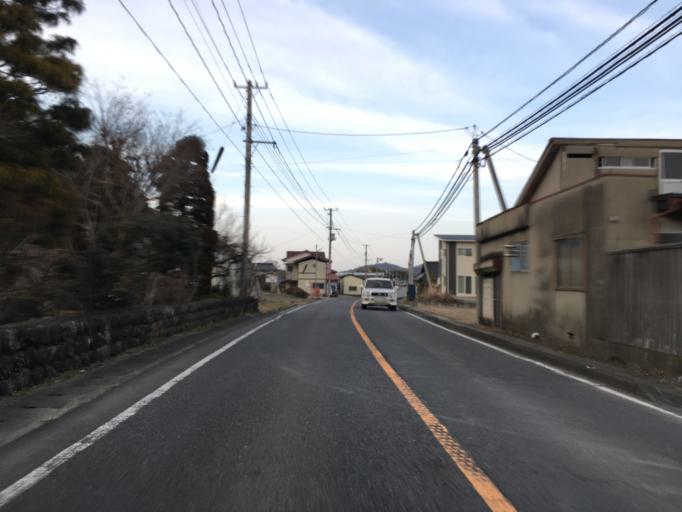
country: JP
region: Ibaraki
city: Daigo
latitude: 36.9071
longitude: 140.4072
